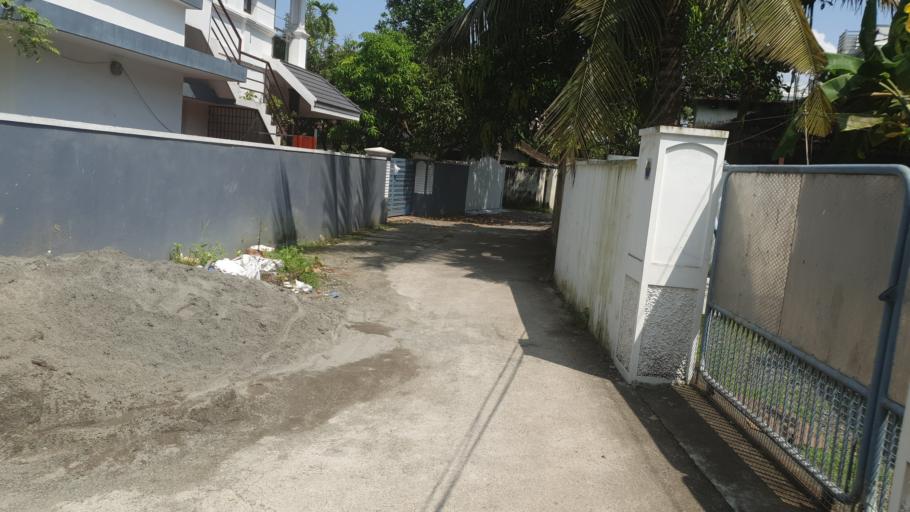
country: IN
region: Kerala
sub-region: Ernakulam
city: Cochin
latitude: 9.9739
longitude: 76.2412
